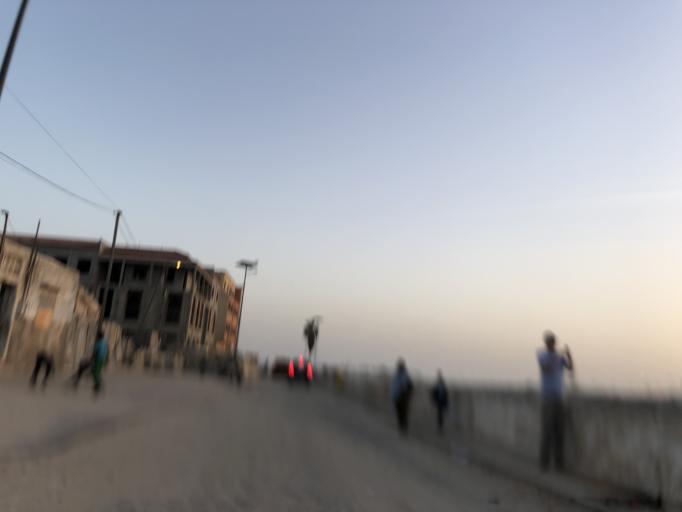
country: SN
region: Saint-Louis
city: Saint-Louis
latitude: 16.0202
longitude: -16.5068
